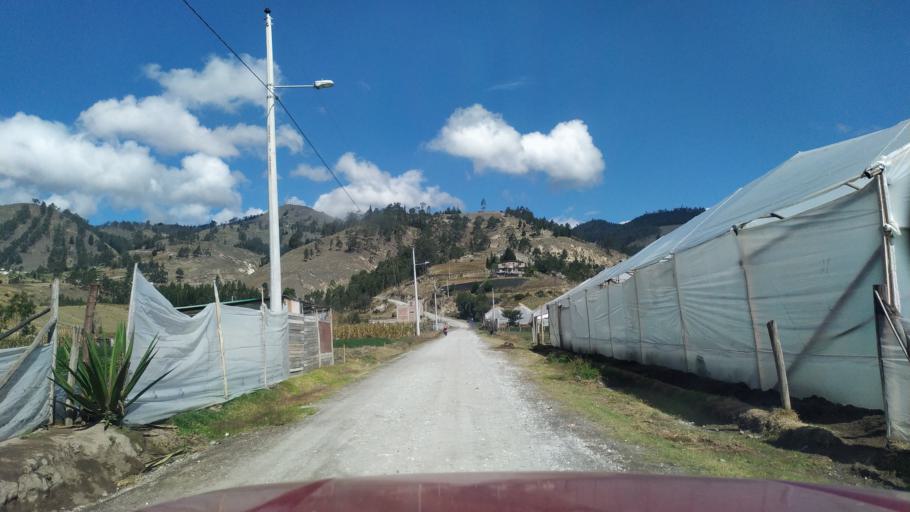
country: EC
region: Chimborazo
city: Riobamba
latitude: -1.6807
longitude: -78.6887
